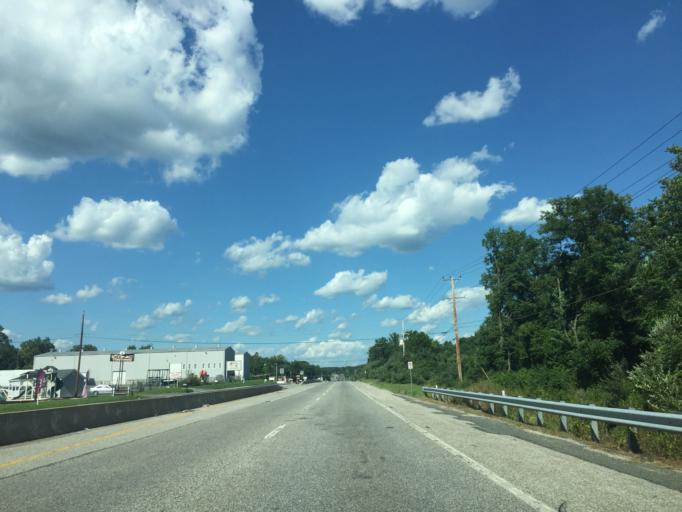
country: US
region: Maryland
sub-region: Baltimore County
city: Kingsville
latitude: 39.4143
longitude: -76.3828
